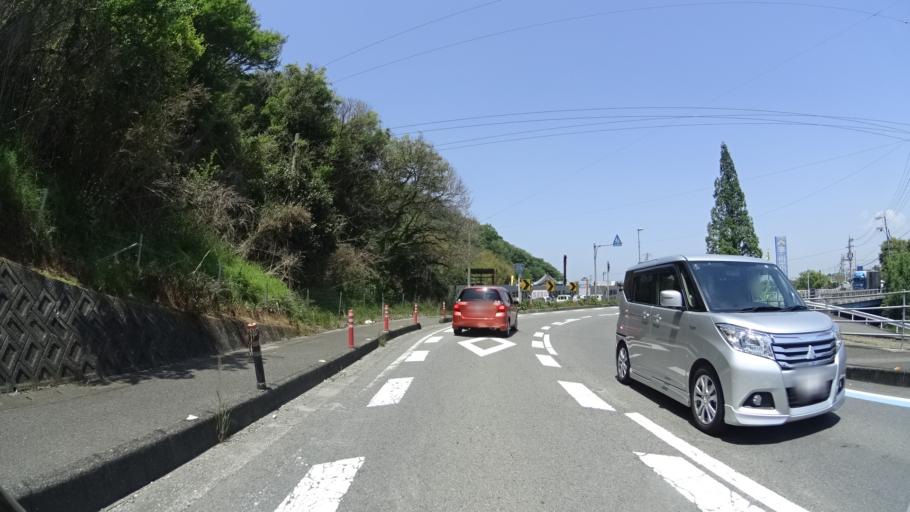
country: JP
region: Ehime
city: Iyo
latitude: 33.7327
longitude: 132.6908
